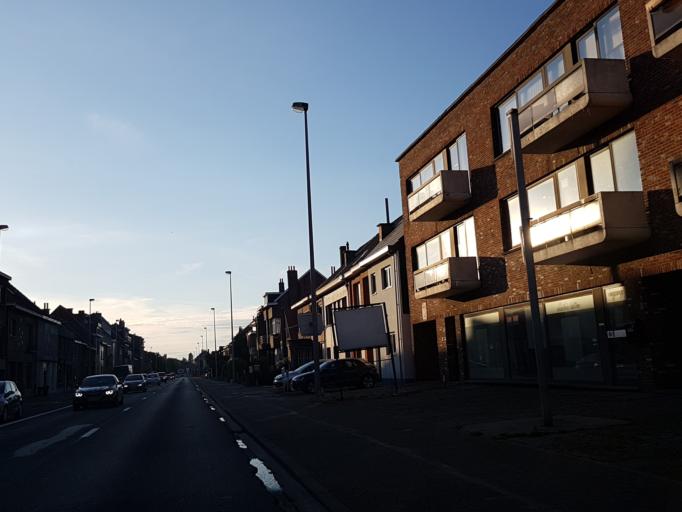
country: BE
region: Flanders
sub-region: Provincie Oost-Vlaanderen
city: Lebbeke
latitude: 51.0051
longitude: 4.1234
